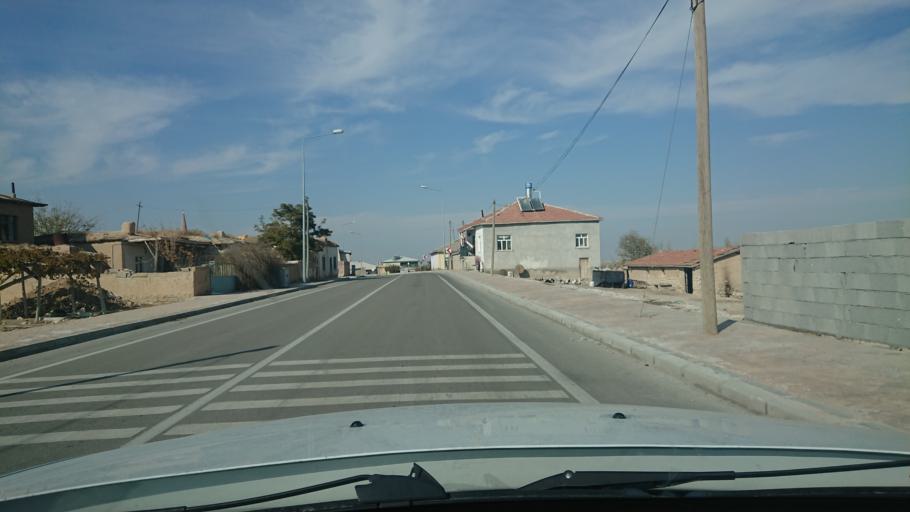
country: TR
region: Aksaray
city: Sultanhani
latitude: 38.2636
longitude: 33.4427
